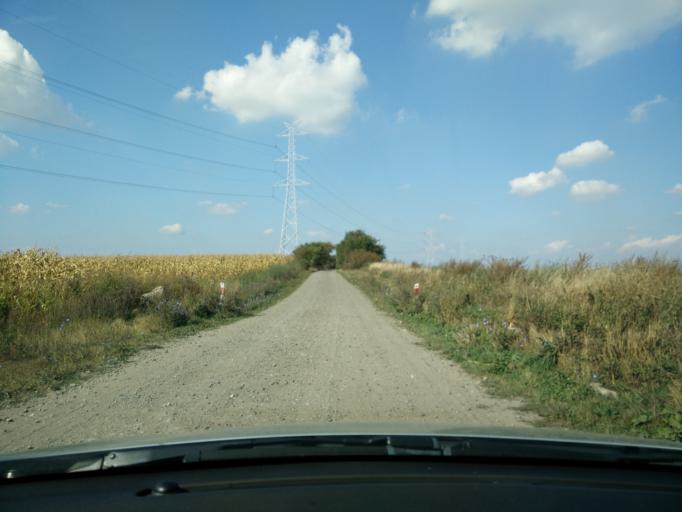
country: PL
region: Greater Poland Voivodeship
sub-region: Powiat sredzki
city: Sroda Wielkopolska
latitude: 52.2557
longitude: 17.1985
